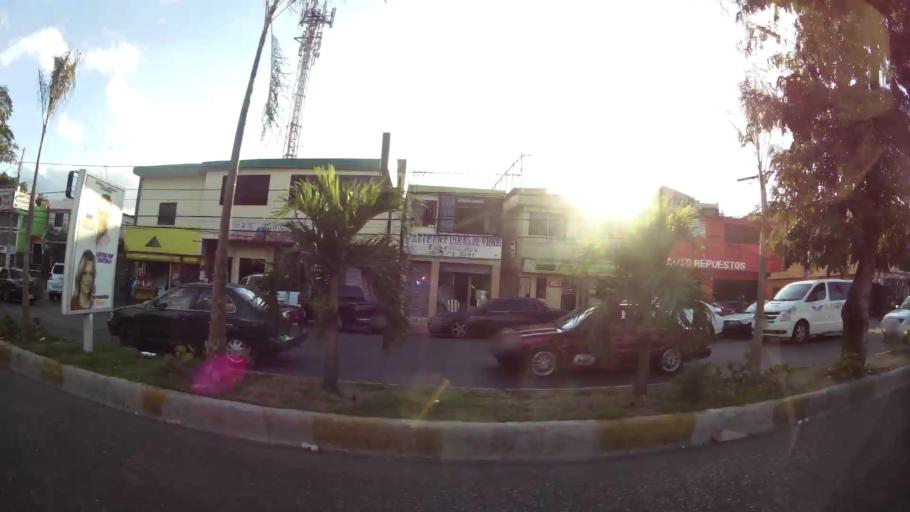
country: DO
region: Santiago
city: Santiago de los Caballeros
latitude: 19.4751
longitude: -70.7156
